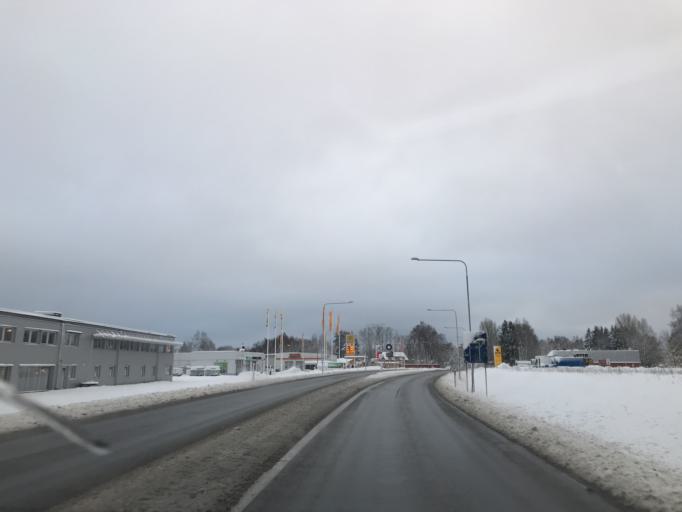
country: SE
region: Vaestra Goetaland
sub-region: Svenljunga Kommun
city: Svenljunga
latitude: 57.5019
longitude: 13.1129
